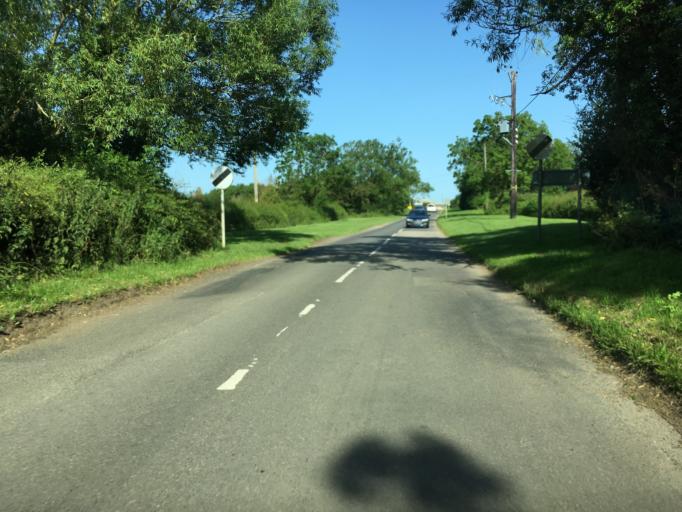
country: GB
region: England
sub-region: Buckinghamshire
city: Steeple Claydon
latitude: 51.9245
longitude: -1.0582
